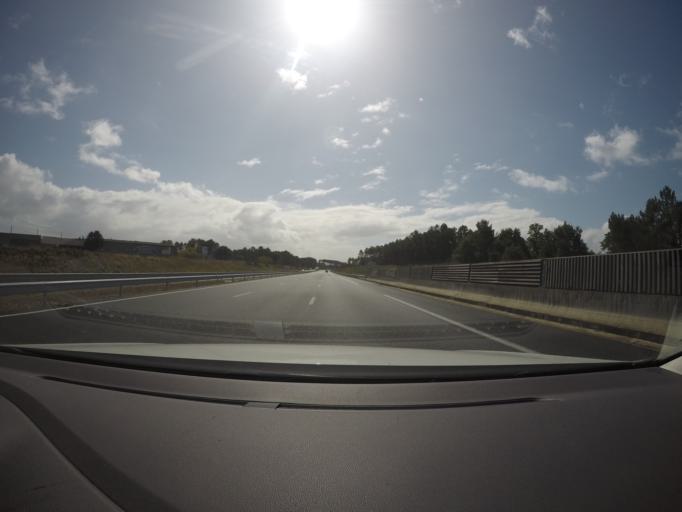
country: FR
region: Aquitaine
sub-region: Departement des Landes
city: Castets
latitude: 43.8884
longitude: -1.1338
